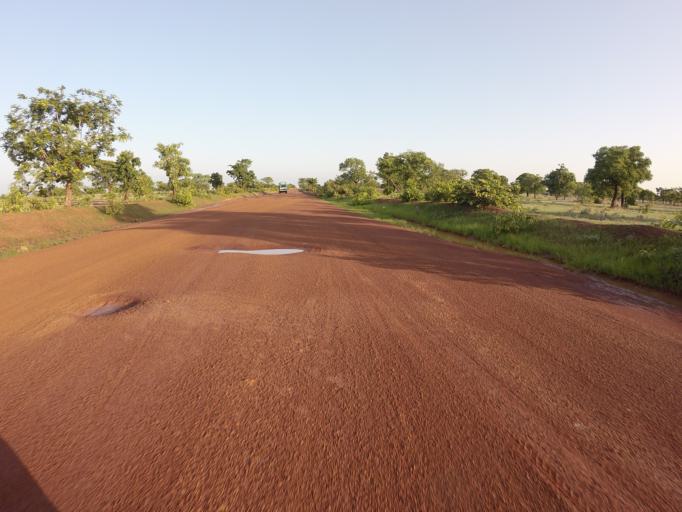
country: TG
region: Savanes
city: Sansanne-Mango
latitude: 10.2725
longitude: -0.0821
